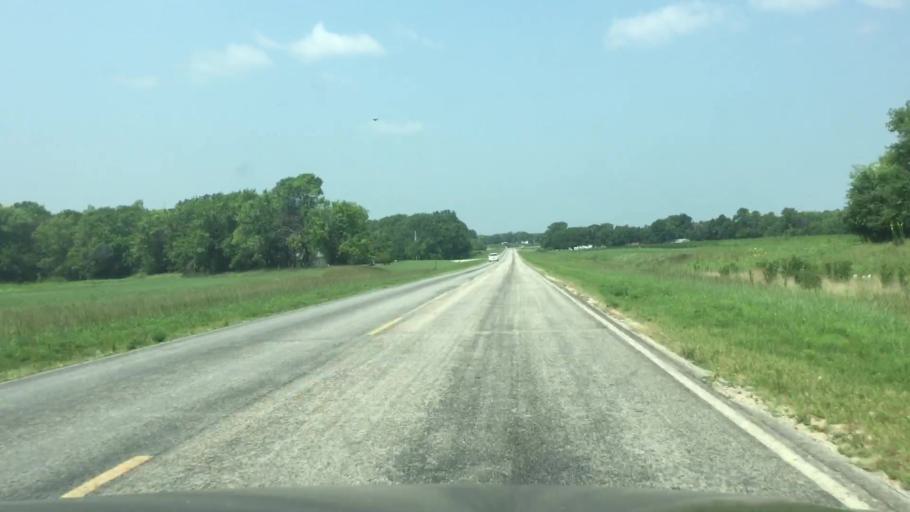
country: US
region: Kansas
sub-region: Allen County
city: Iola
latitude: 37.8851
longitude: -95.4022
